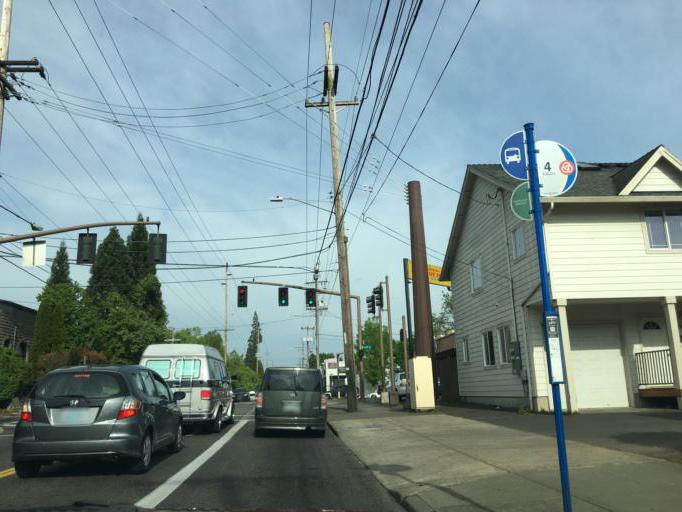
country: US
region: Oregon
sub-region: Multnomah County
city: Lents
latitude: 45.5054
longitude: -122.6021
